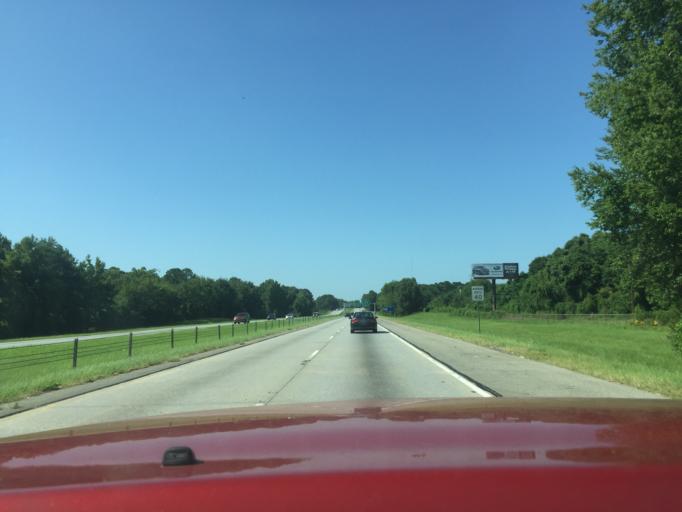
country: US
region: Georgia
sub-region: Chatham County
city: Savannah
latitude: 32.0605
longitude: -81.1393
